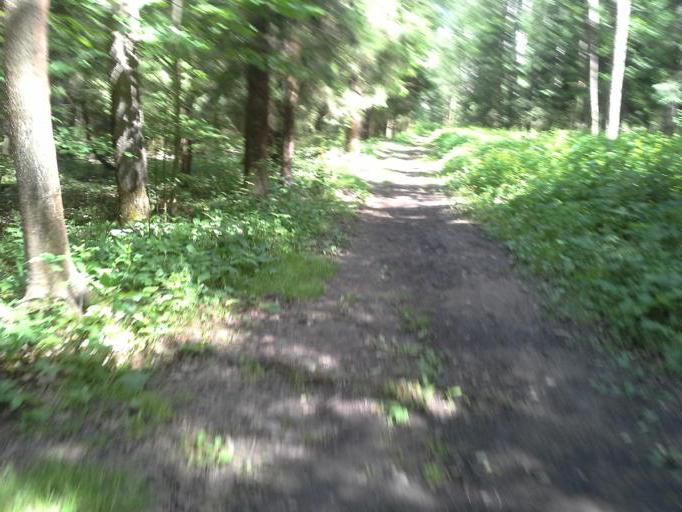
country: RU
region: Moscow
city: Tolstopal'tsevo
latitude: 55.6165
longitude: 37.2470
